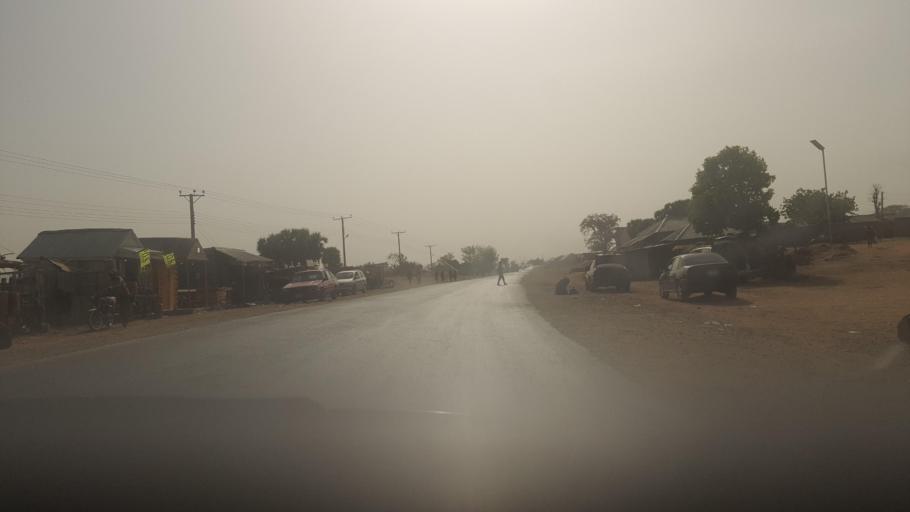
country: NG
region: Bauchi
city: Dindima
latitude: 10.2613
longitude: 9.9953
